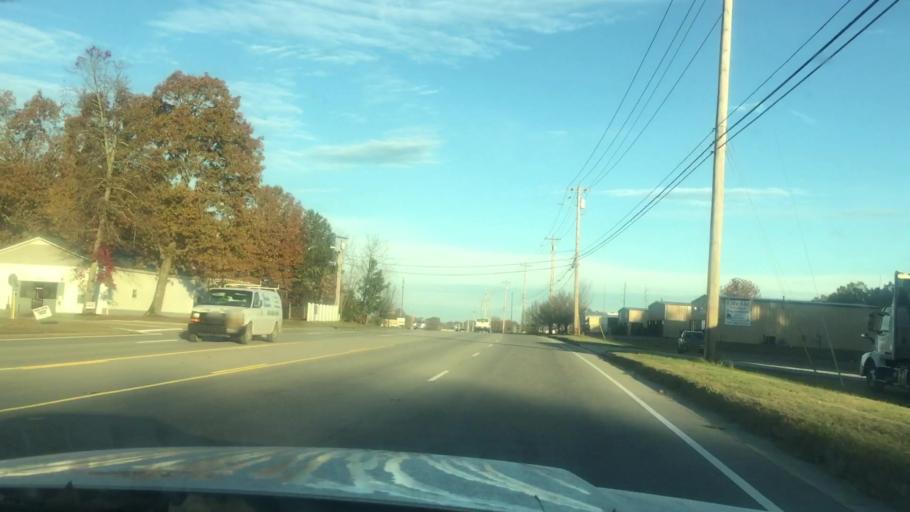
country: US
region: Tennessee
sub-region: Coffee County
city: Tullahoma
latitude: 35.3455
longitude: -86.1950
